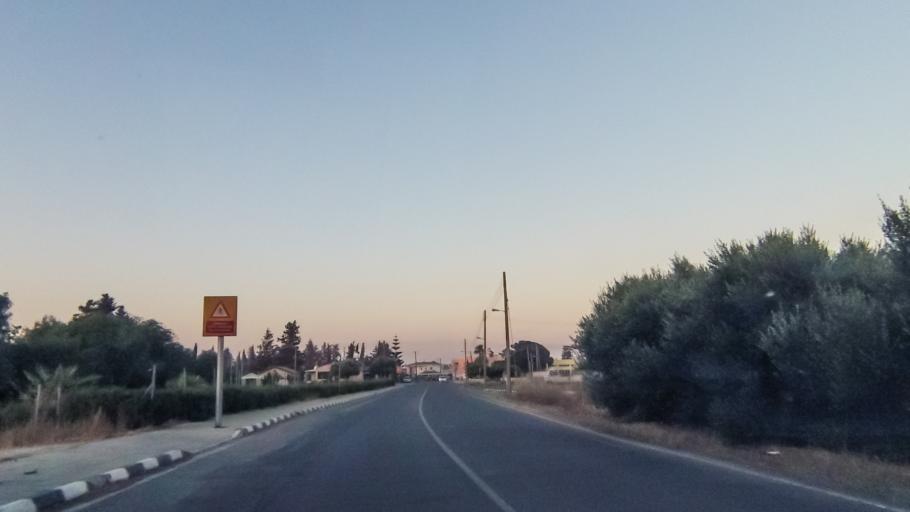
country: CY
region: Larnaka
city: Kolossi
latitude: 34.6383
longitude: 32.9588
